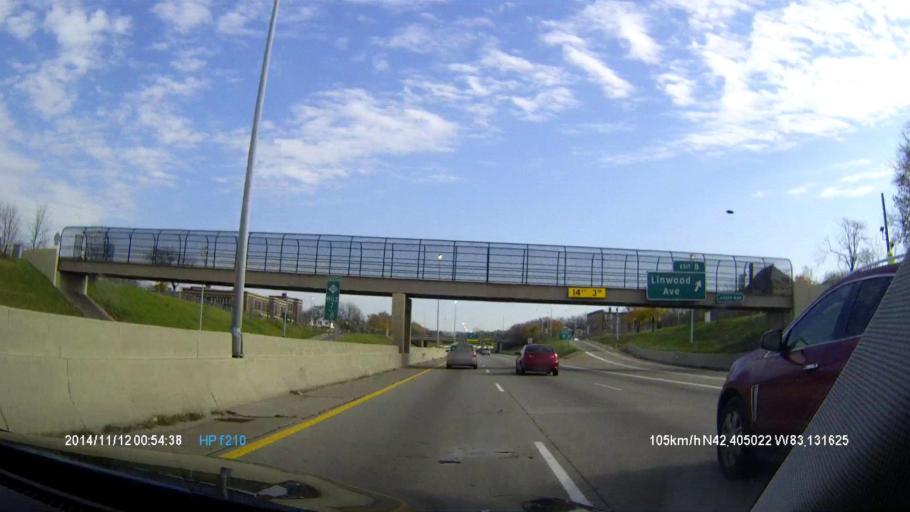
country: US
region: Michigan
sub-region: Wayne County
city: Highland Park
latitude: 42.4050
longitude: -83.1313
